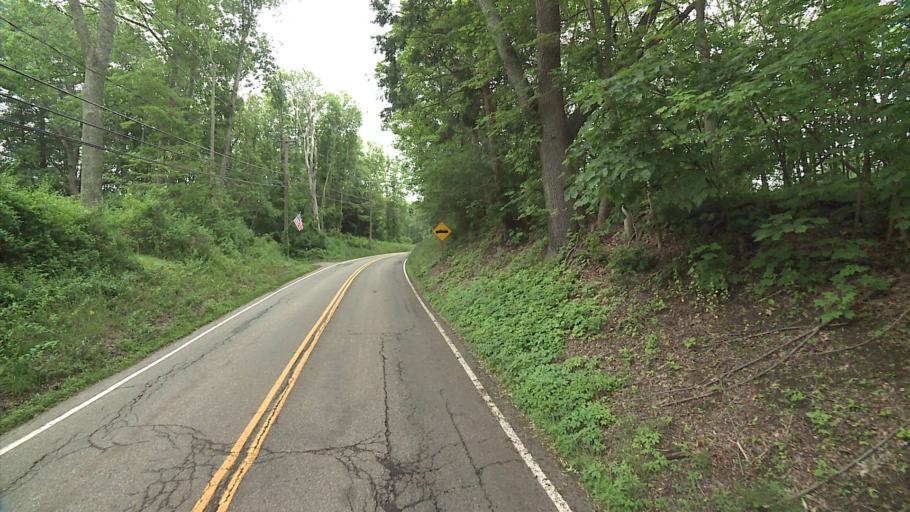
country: US
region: Connecticut
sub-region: Tolland County
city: Coventry Lake
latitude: 41.7306
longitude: -72.3710
